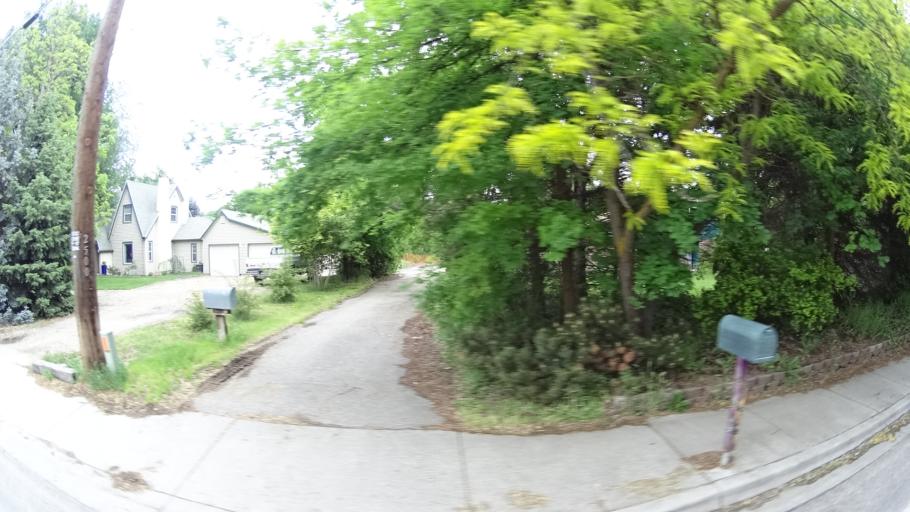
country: US
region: Idaho
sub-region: Ada County
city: Garden City
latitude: 43.6427
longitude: -116.2334
